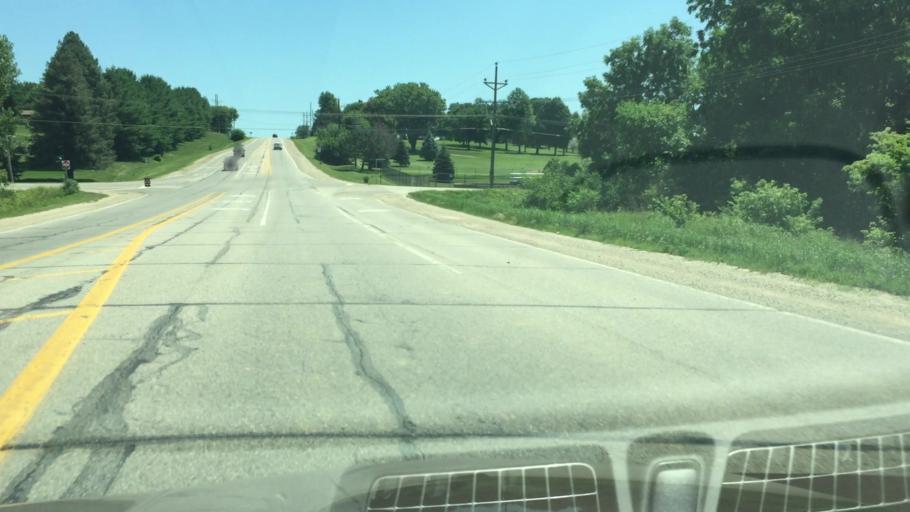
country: US
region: Iowa
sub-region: Linn County
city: Mount Vernon
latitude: 41.9166
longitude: -91.4110
